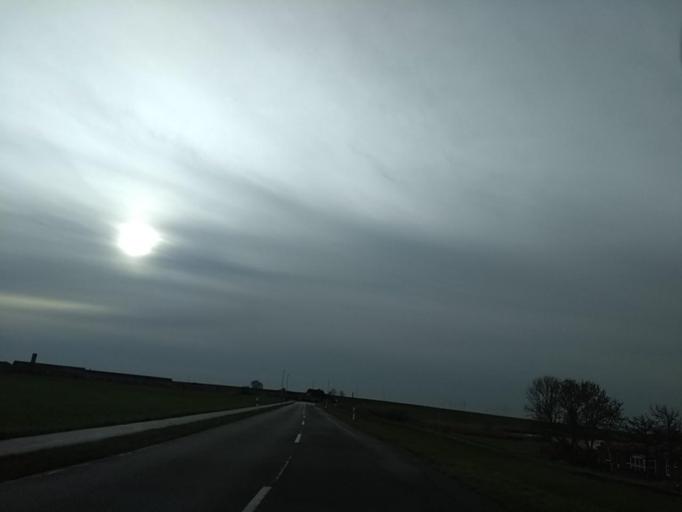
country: NL
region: Groningen
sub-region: Gemeente Delfzijl
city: Delfzijl
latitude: 53.3434
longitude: 7.0528
